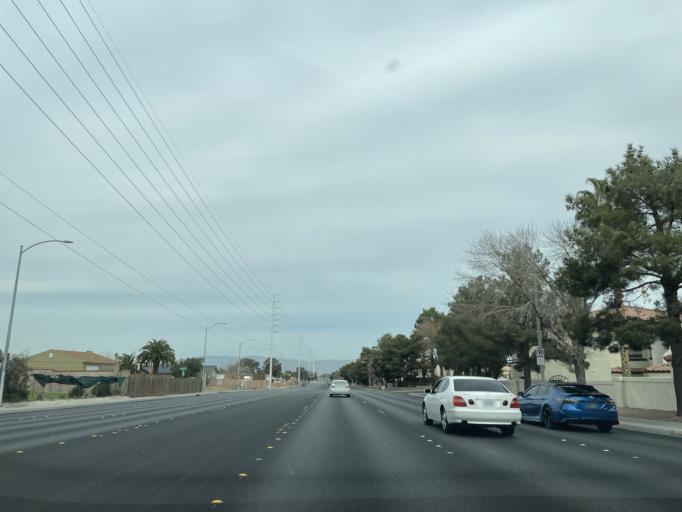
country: US
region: Nevada
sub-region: Clark County
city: Whitney
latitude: 36.0450
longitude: -115.1182
